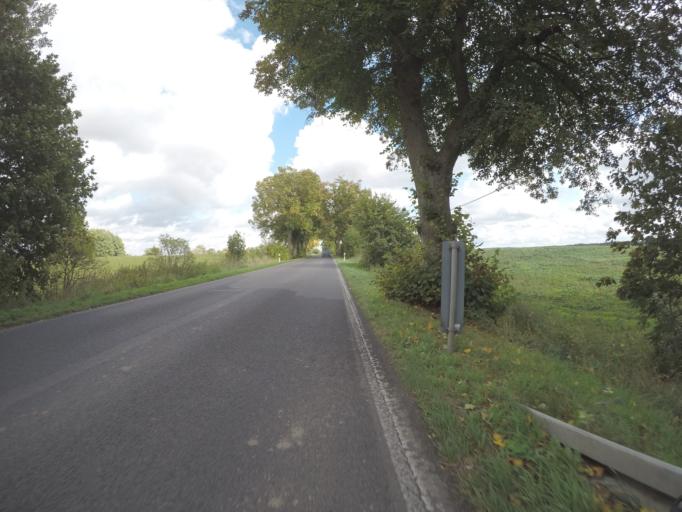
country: DE
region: Brandenburg
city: Altlandsberg
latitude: 52.5780
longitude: 13.7553
